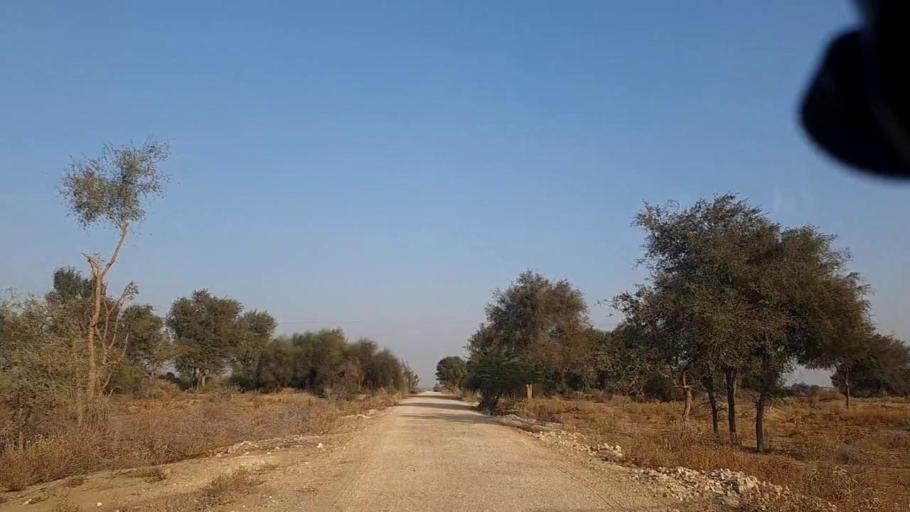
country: PK
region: Sindh
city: Khanpur
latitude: 27.6134
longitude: 69.5308
